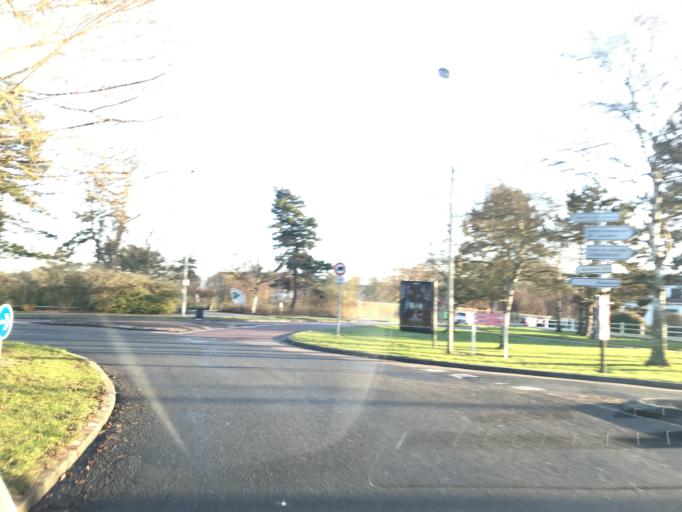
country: FR
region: Haute-Normandie
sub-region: Departement de la Seine-Maritime
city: Le Grand-Quevilly
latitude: 49.4050
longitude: 1.0549
